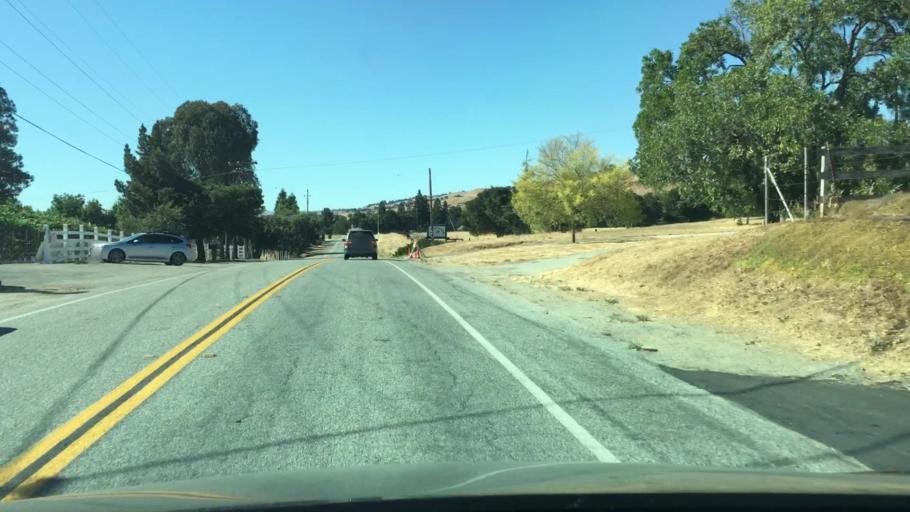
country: US
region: California
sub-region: Santa Clara County
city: San Martin
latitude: 37.0842
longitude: -121.5653
